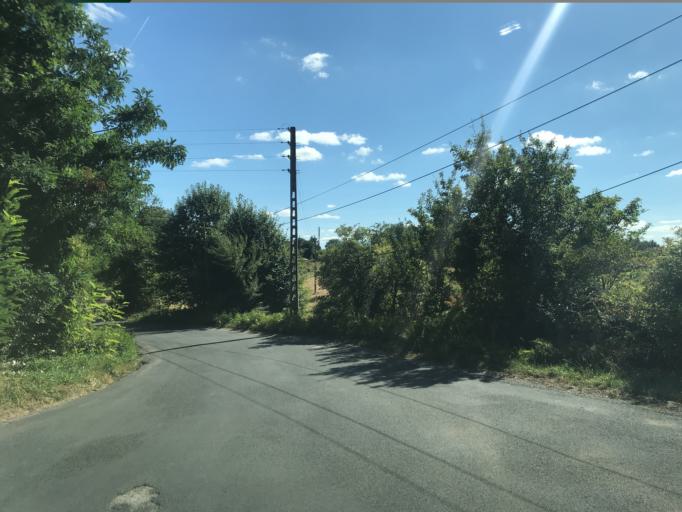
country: FR
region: Aquitaine
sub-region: Departement de la Dordogne
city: Sarlat-la-Caneda
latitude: 44.9210
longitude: 1.1977
